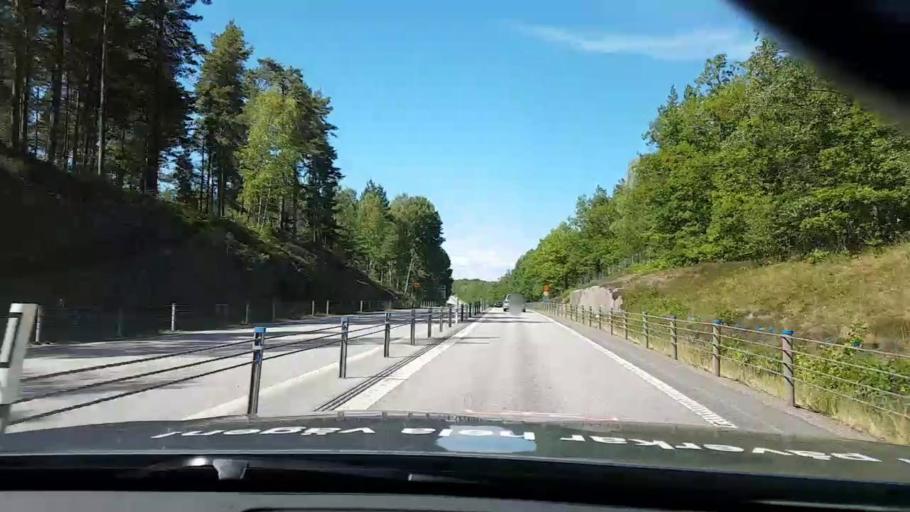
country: SE
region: Kalmar
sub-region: Vasterviks Kommun
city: Gamleby
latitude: 57.8349
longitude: 16.4422
